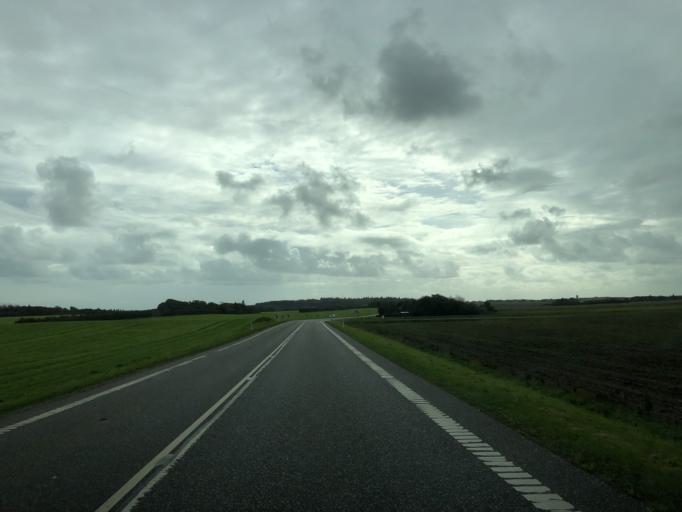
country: DK
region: North Denmark
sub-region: Thisted Kommune
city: Hurup
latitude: 56.7282
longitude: 8.4283
